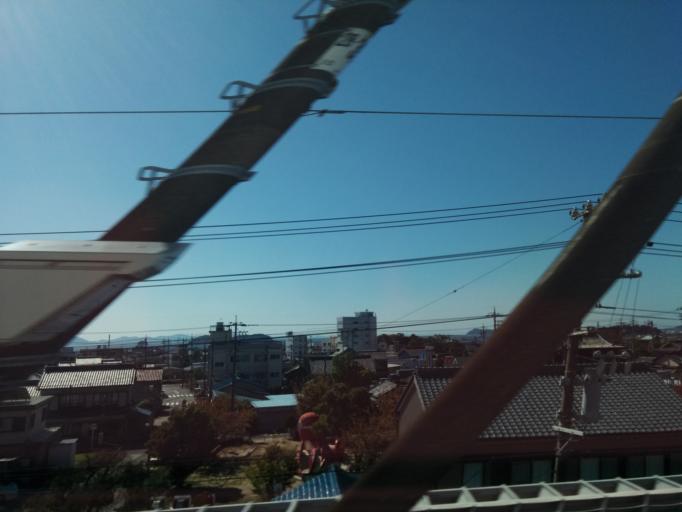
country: JP
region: Aichi
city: Gamagori
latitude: 34.8197
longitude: 137.2518
